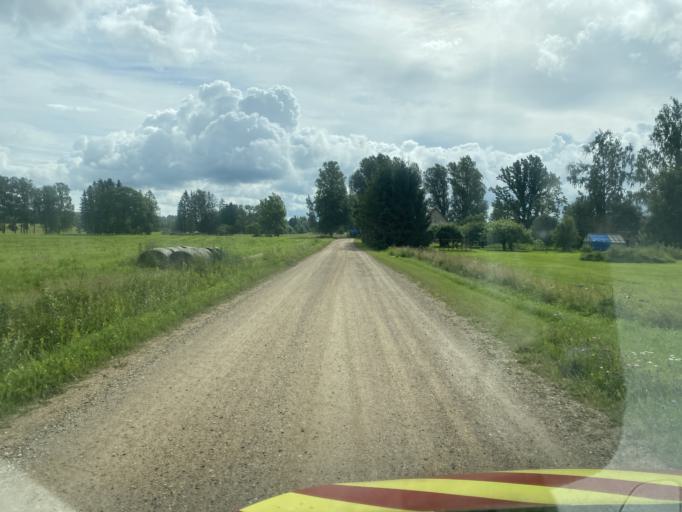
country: EE
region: Viljandimaa
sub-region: Karksi vald
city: Karksi-Nuia
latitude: 58.0579
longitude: 25.5467
